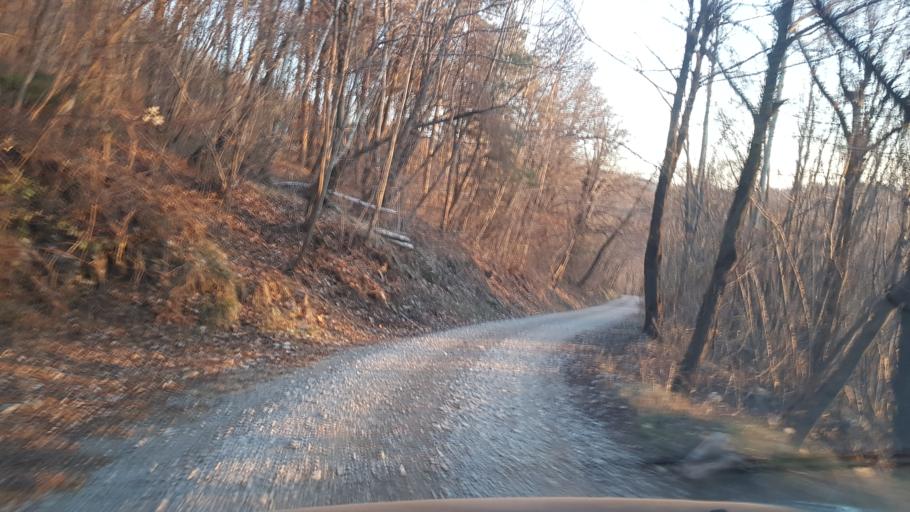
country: SI
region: Nova Gorica
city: Kromberk
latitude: 46.0121
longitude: 13.6992
